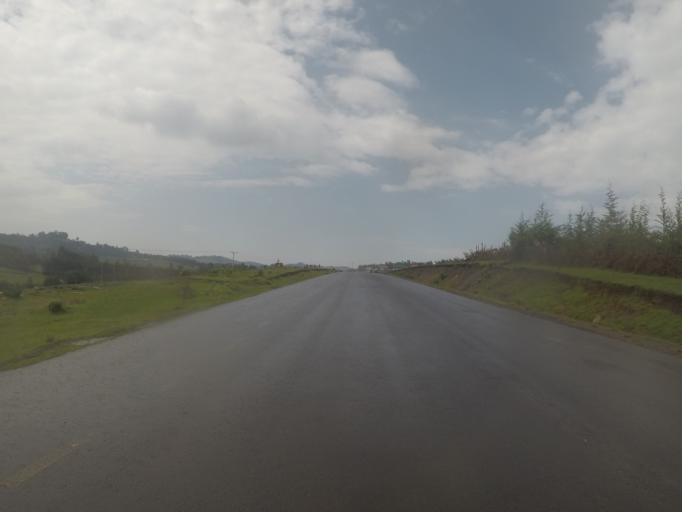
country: ET
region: Amhara
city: Debark'
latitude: 13.1317
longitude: 37.8916
